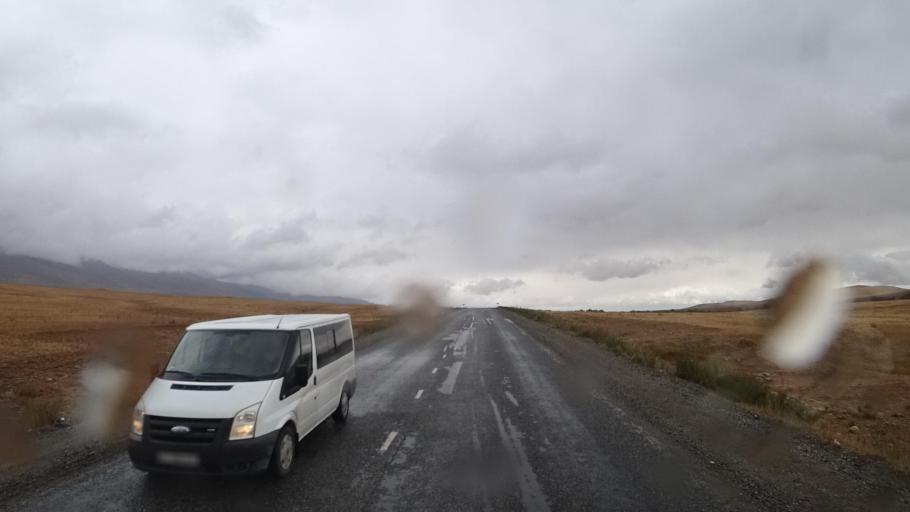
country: KG
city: Sosnovka
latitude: 42.2161
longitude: 73.6845
